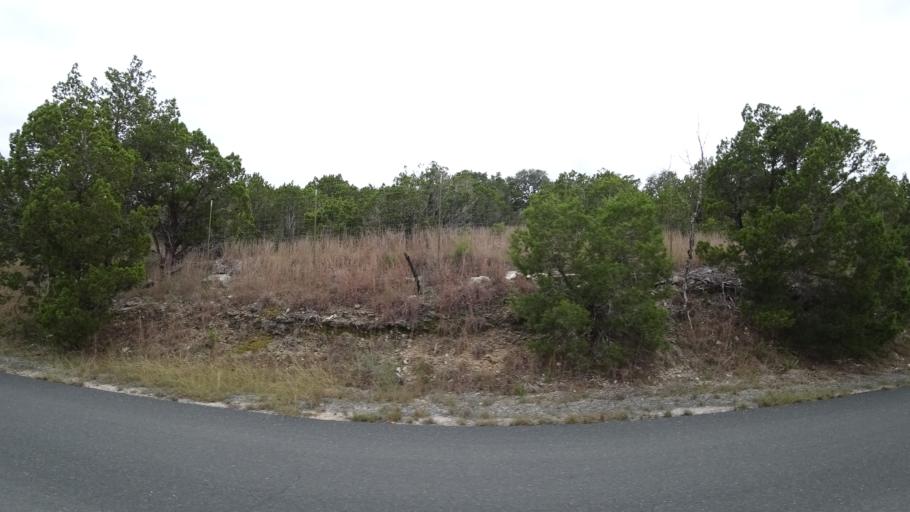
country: US
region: Texas
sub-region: Travis County
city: Bee Cave
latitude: 30.3485
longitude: -97.9392
